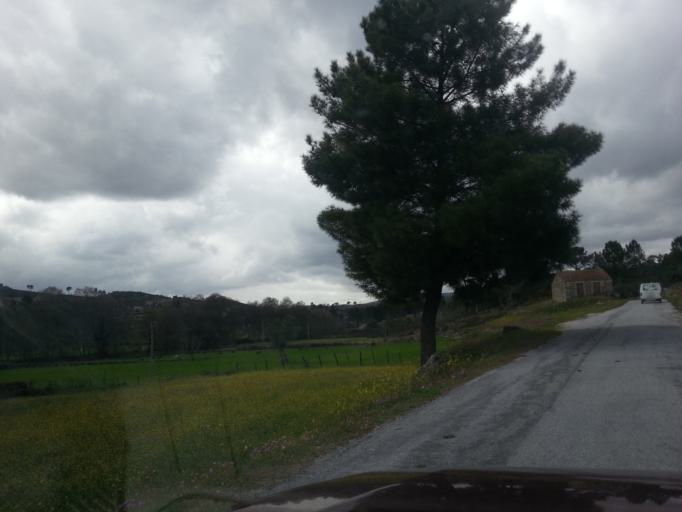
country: PT
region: Guarda
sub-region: Fornos de Algodres
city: Fornos de Algodres
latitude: 40.5840
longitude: -7.5526
